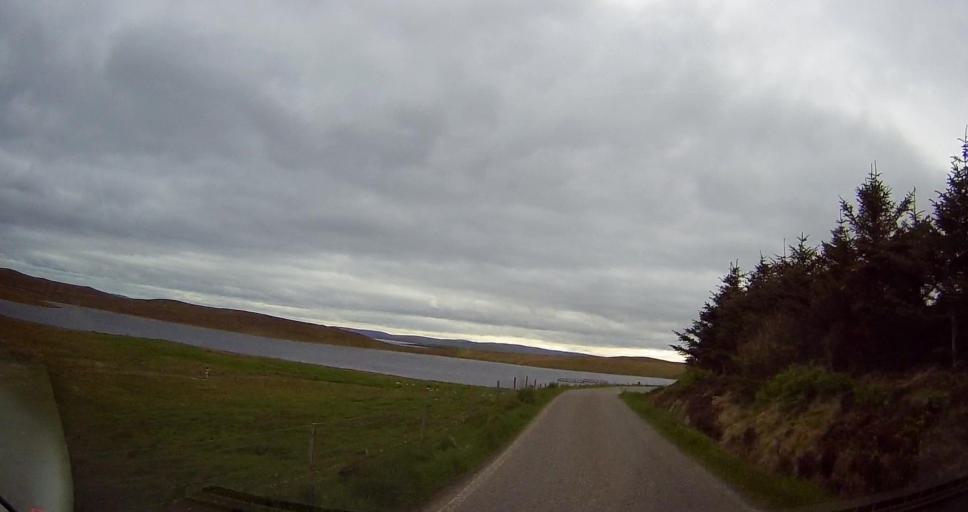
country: GB
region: Scotland
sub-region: Shetland Islands
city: Shetland
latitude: 60.5007
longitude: -1.0666
